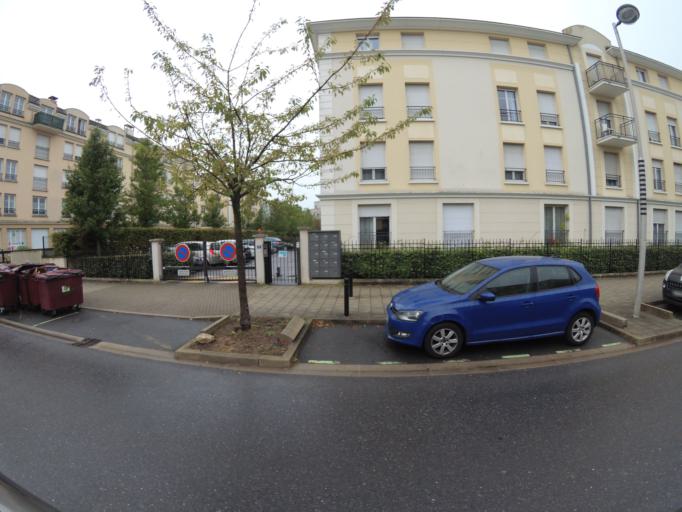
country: FR
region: Ile-de-France
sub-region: Departement de Seine-et-Marne
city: Bussy-Saint-Georges
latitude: 48.8344
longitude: 2.7087
